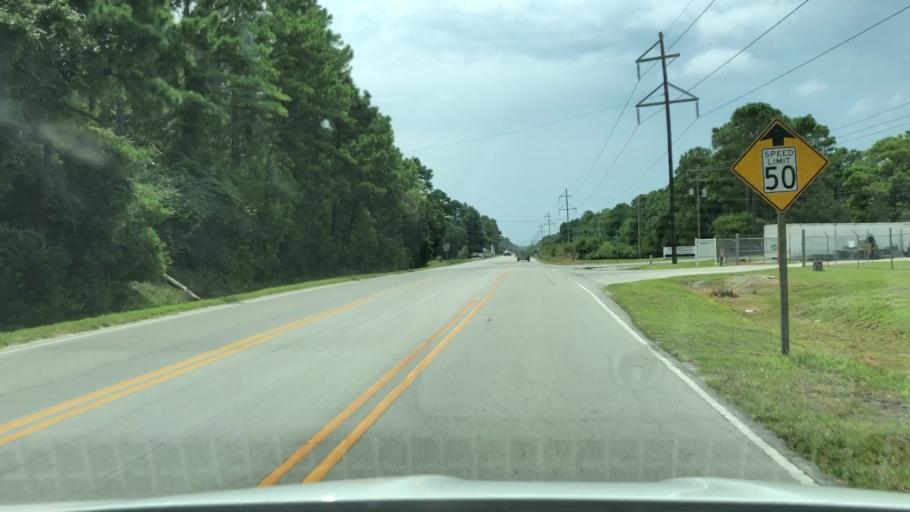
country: US
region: North Carolina
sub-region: Carteret County
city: Newport
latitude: 34.7555
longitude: -76.8747
